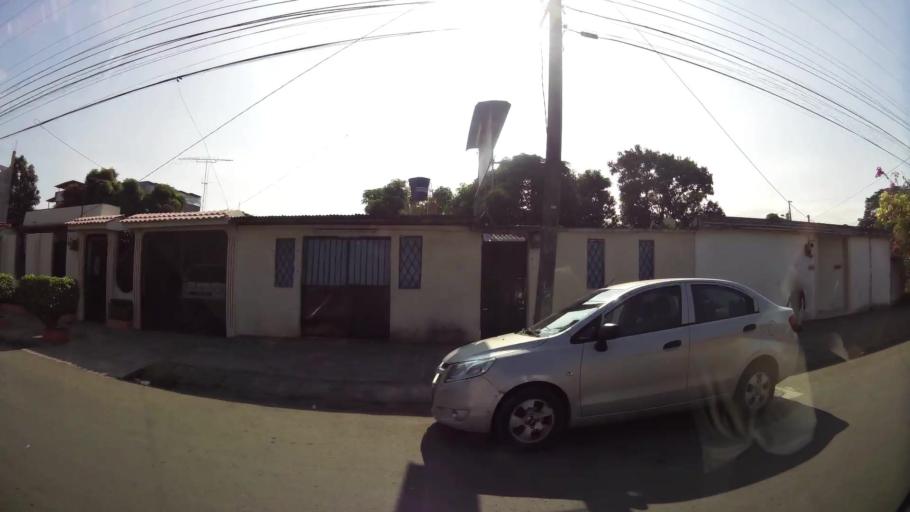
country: EC
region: Guayas
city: Eloy Alfaro
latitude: -2.1883
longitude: -79.8217
